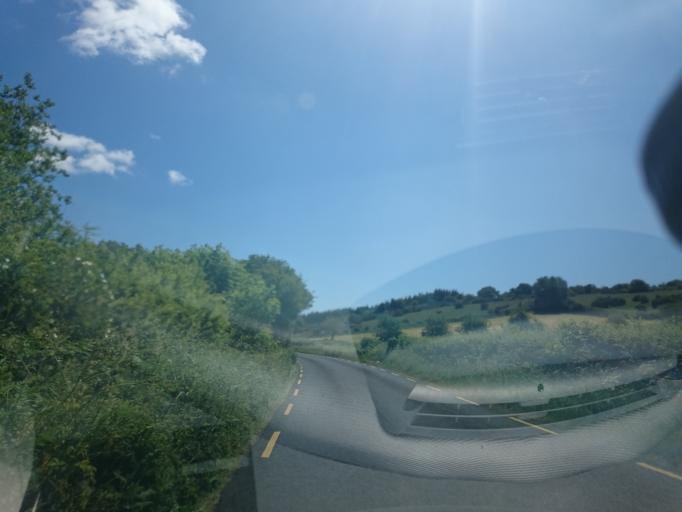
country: IE
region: Leinster
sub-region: Kilkenny
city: Graiguenamanagh
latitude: 52.5853
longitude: -6.9578
